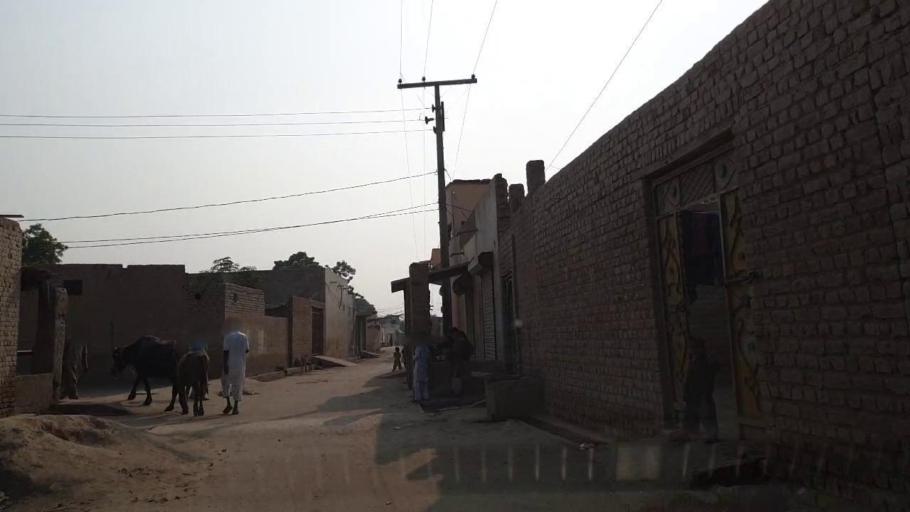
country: PK
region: Sindh
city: Bhan
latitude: 26.5792
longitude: 67.7298
